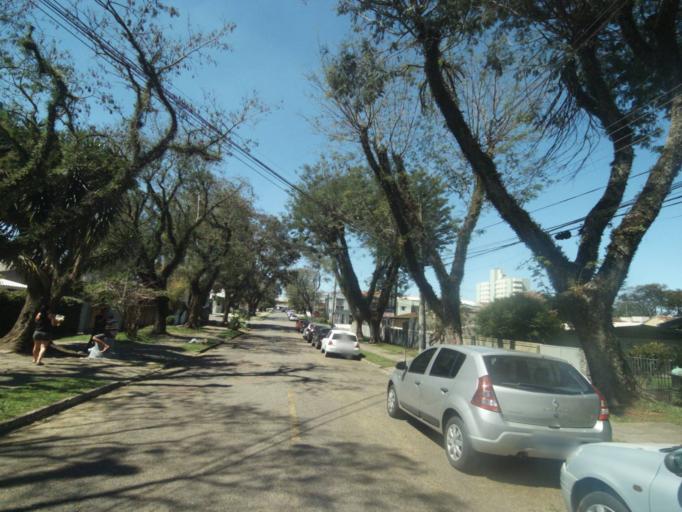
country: BR
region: Parana
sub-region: Curitiba
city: Curitiba
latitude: -25.4049
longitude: -49.2433
